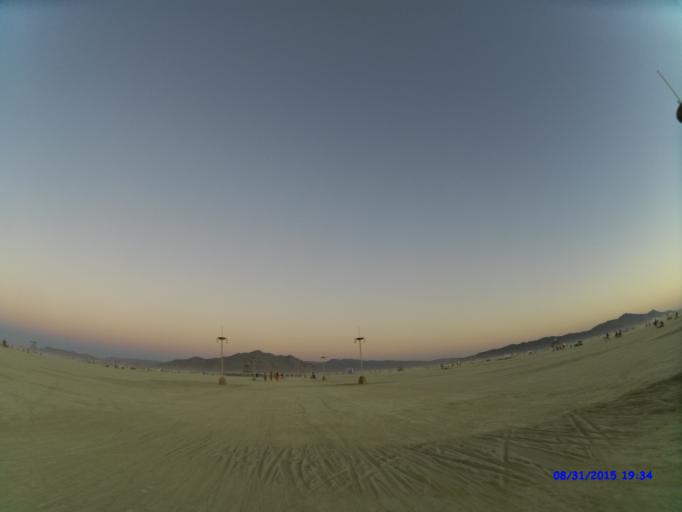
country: US
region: Nevada
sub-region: Pershing County
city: Lovelock
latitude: 40.7854
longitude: -119.2053
